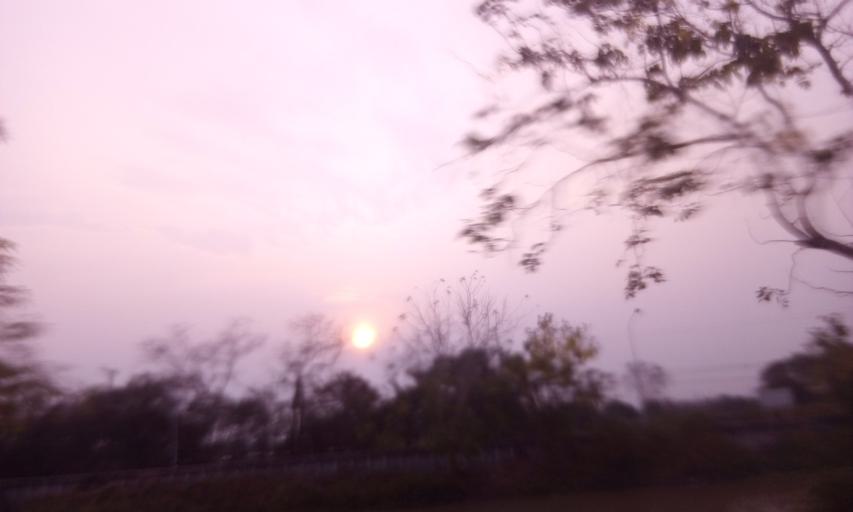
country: TH
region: Bangkok
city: Nong Chok
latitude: 13.9533
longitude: 100.8950
